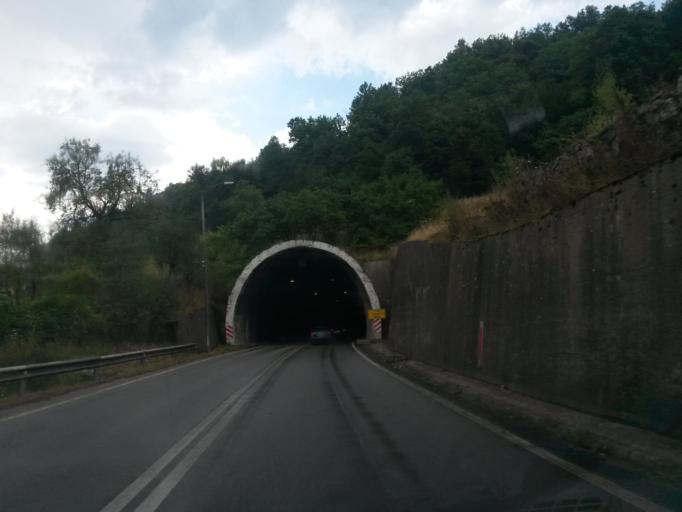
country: BA
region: Federation of Bosnia and Herzegovina
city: Maglaj
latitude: 44.5313
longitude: 18.0865
